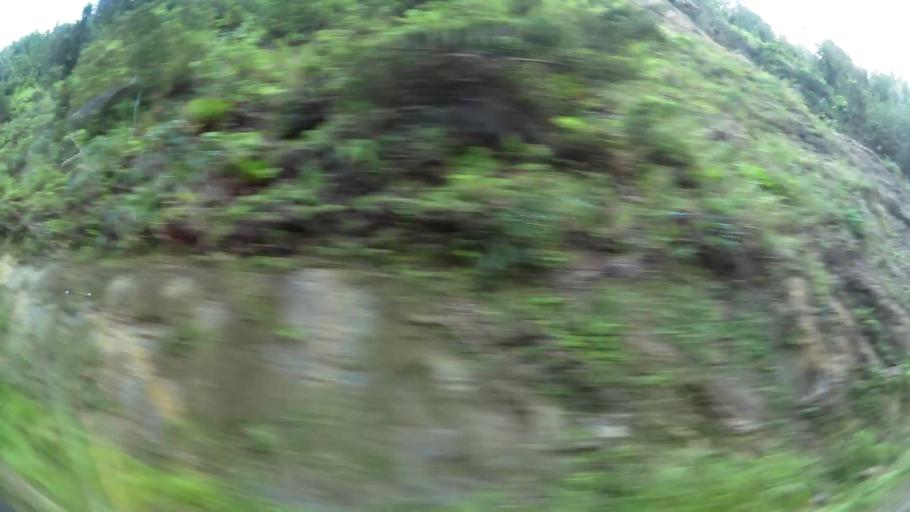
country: GP
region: Guadeloupe
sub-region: Guadeloupe
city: Bouillante
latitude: 16.1800
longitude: -61.7266
